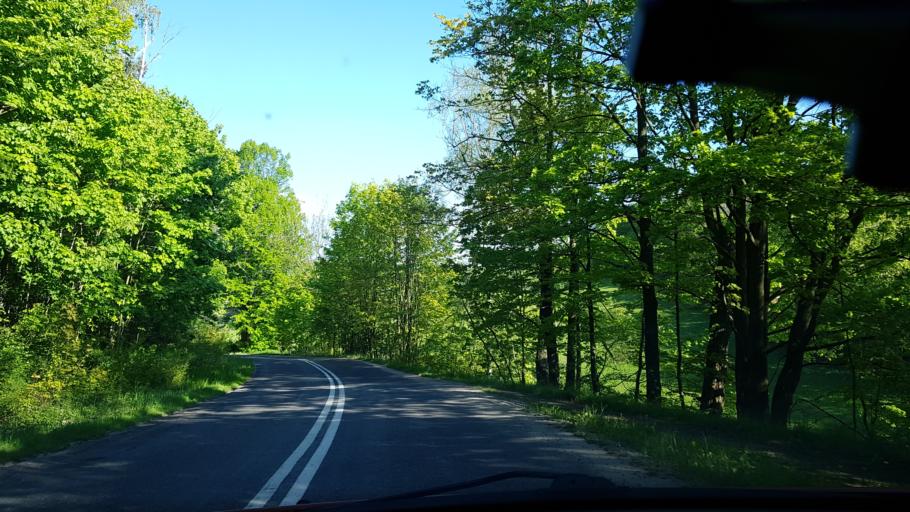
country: PL
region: Lower Silesian Voivodeship
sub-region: Powiat klodzki
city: Bozkow
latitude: 50.5742
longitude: 16.6045
